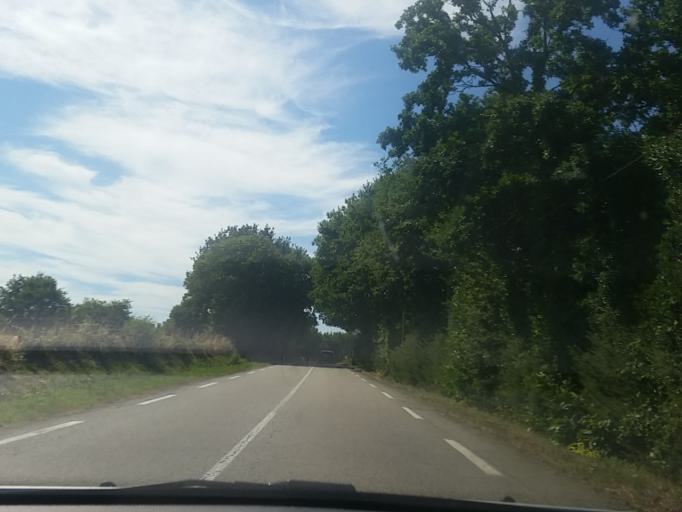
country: FR
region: Pays de la Loire
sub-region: Departement de la Loire-Atlantique
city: Chauve
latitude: 47.1901
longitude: -1.9920
